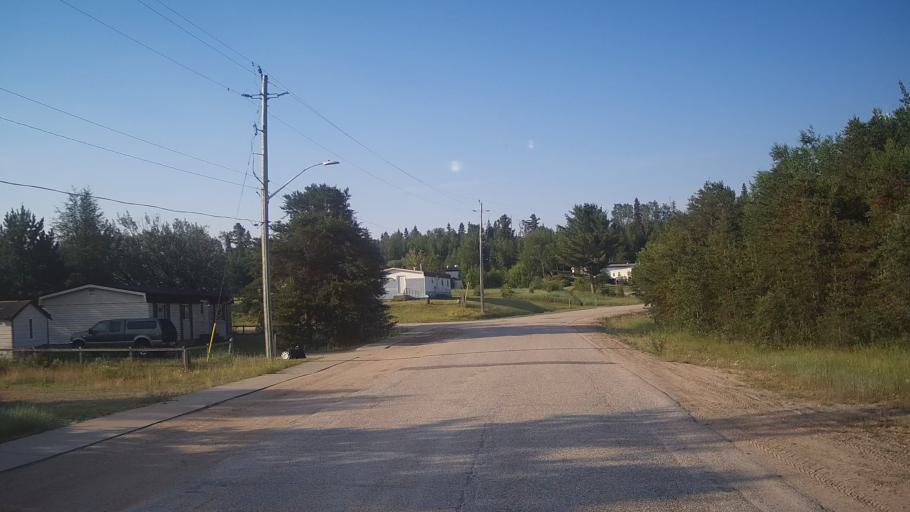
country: CA
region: Ontario
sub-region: Rainy River District
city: Atikokan
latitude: 49.4033
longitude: -91.6573
